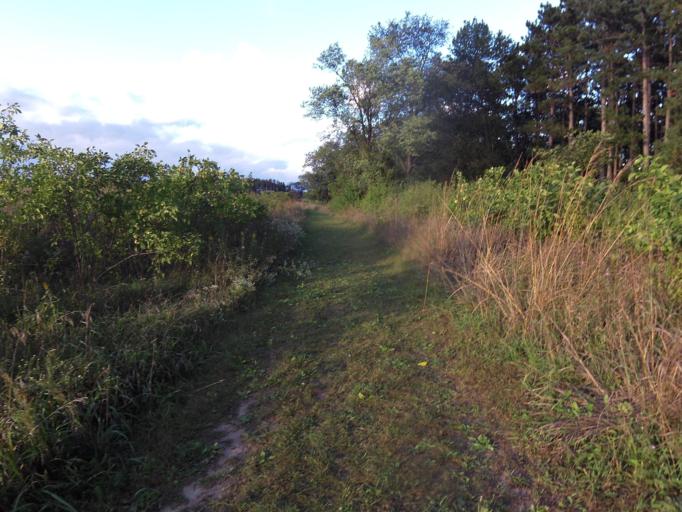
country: US
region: Minnesota
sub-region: Washington County
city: Lake Saint Croix Beach
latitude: 44.9350
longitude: -92.7875
